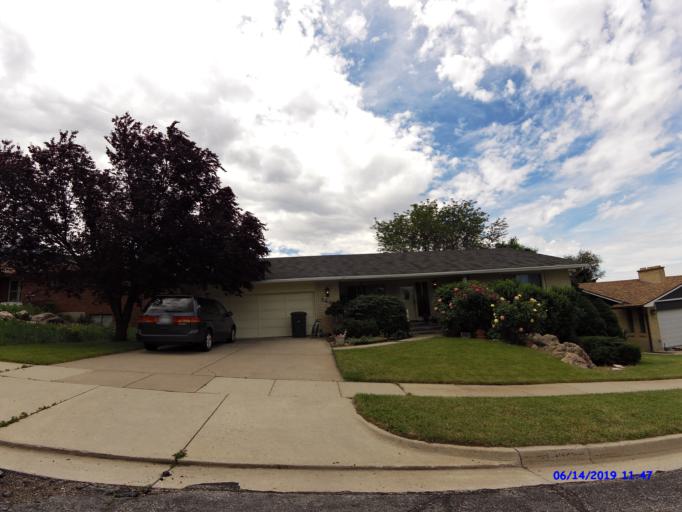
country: US
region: Utah
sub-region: Weber County
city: Ogden
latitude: 41.2538
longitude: -111.9409
